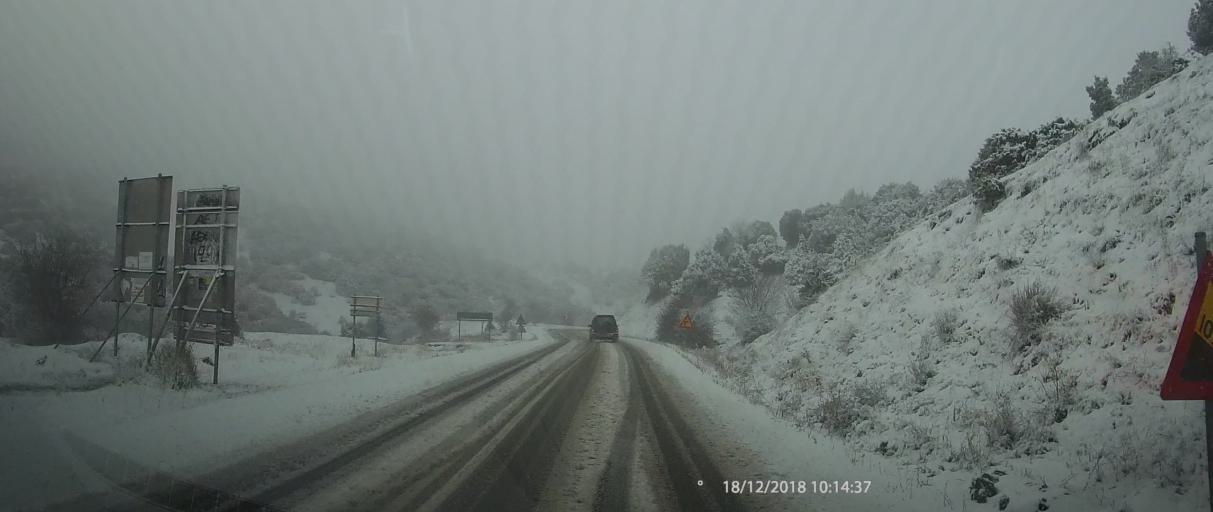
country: GR
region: Thessaly
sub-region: Nomos Larisis
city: Livadi
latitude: 40.1096
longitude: 22.2023
